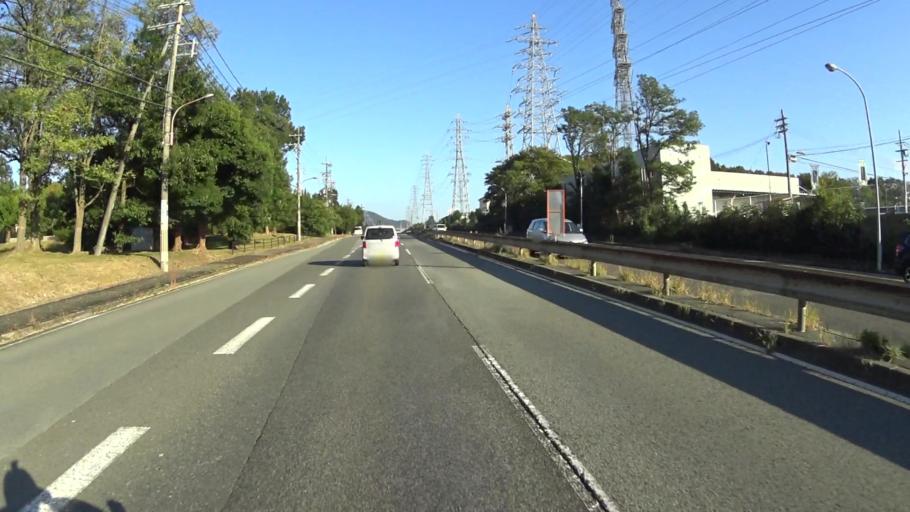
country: JP
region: Kyoto
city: Fukuchiyama
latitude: 35.2911
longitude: 135.1611
